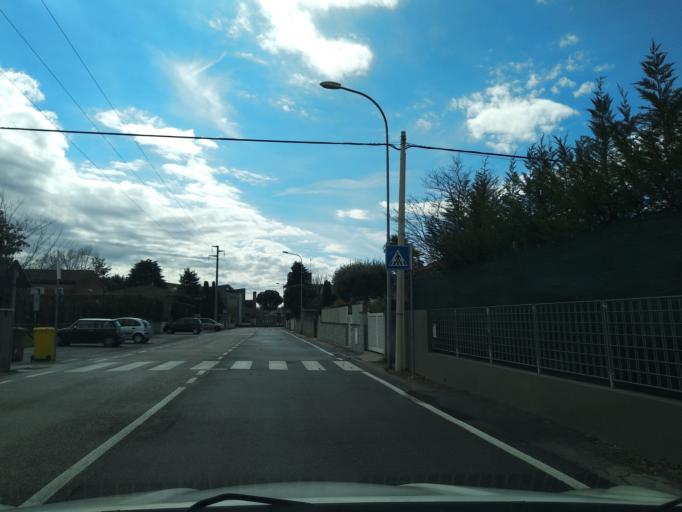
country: IT
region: Veneto
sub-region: Provincia di Vicenza
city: Monticello Conte Otto
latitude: 45.6042
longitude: 11.5719
